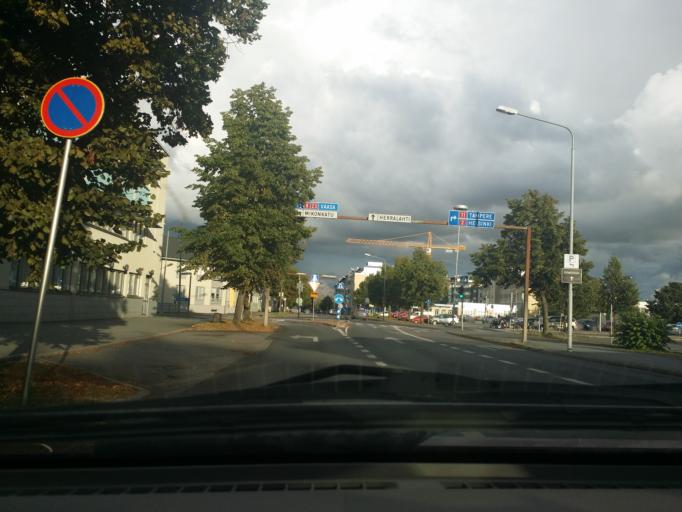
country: FI
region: Satakunta
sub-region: Pori
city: Pori
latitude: 61.4816
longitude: 21.7985
